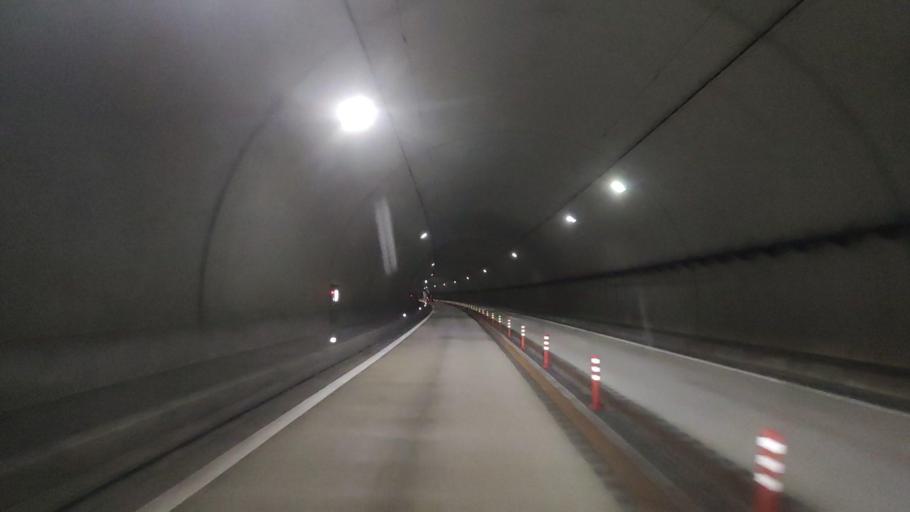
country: JP
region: Wakayama
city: Tanabe
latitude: 33.5627
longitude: 135.5019
